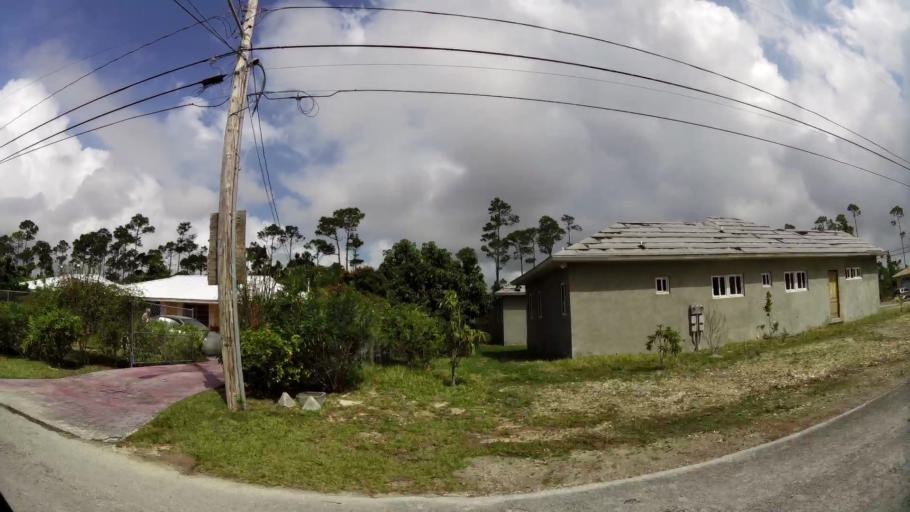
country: BS
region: Freeport
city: Lucaya
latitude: 26.5472
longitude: -78.5859
